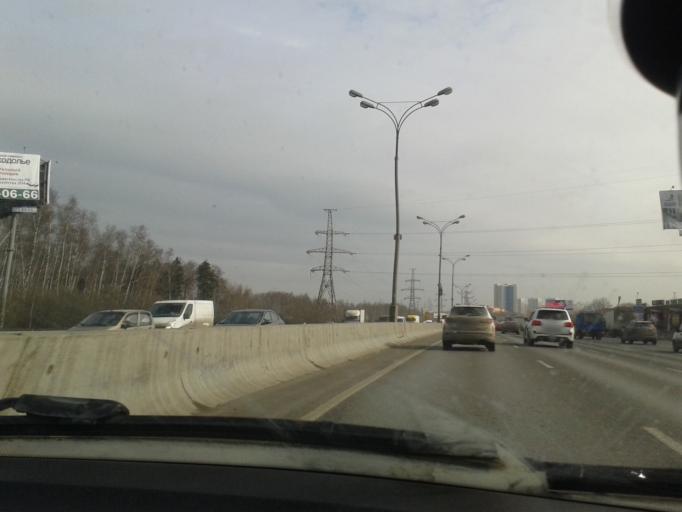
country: RU
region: Moscow
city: Businovo
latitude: 55.9019
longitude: 37.5189
